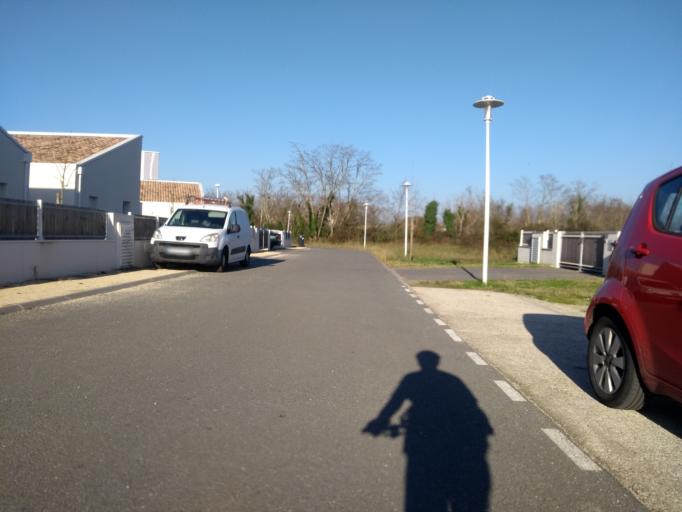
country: FR
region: Aquitaine
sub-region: Departement de la Gironde
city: Martillac
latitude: 44.7292
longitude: -0.5160
